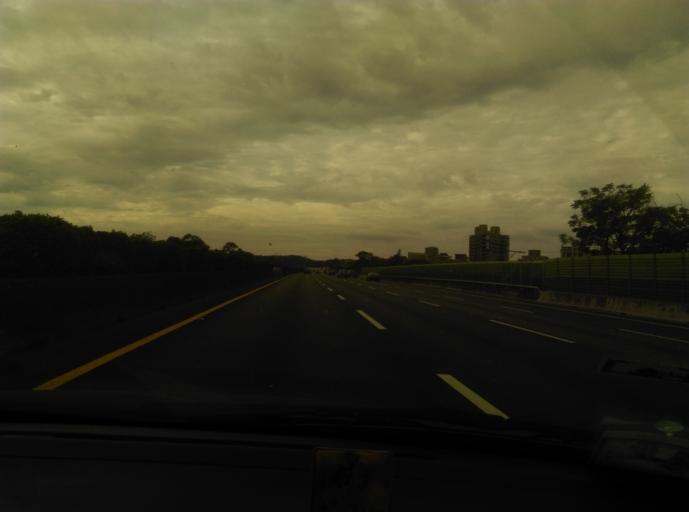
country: TW
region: Taiwan
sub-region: Taoyuan
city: Taoyuan
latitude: 24.9362
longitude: 121.3413
